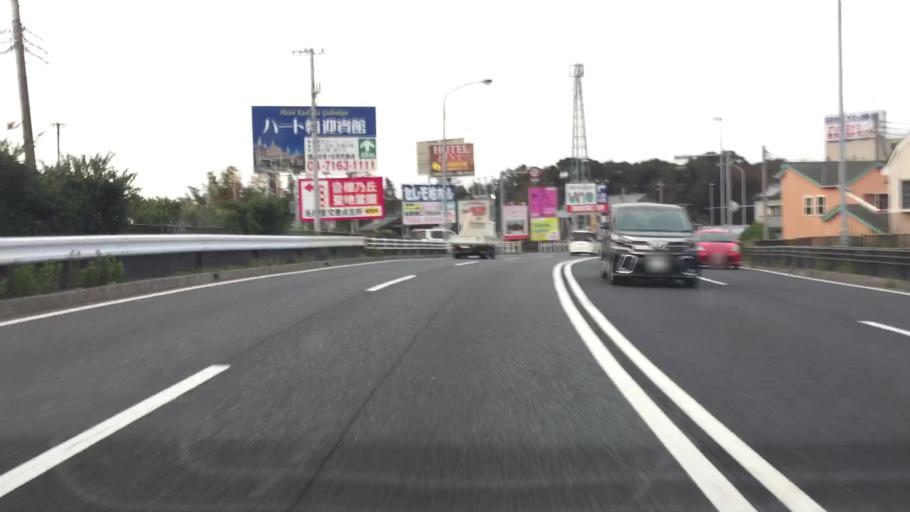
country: JP
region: Chiba
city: Kashiwa
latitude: 35.8380
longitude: 139.9400
